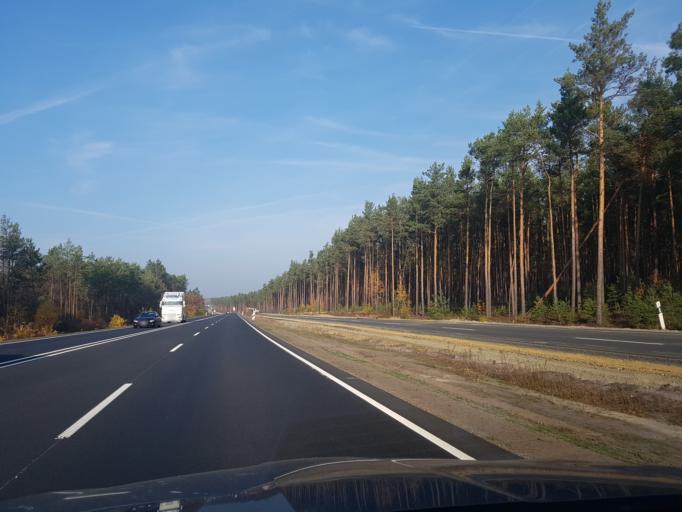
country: DE
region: Brandenburg
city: Elsterwerda
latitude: 51.4928
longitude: 13.4749
